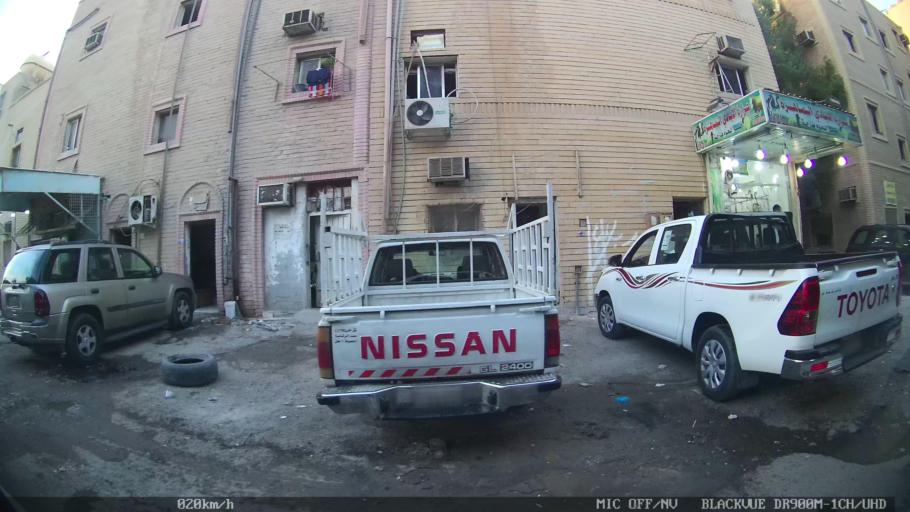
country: KW
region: Al Farwaniyah
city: Janub as Surrah
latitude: 29.2887
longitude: 47.9788
